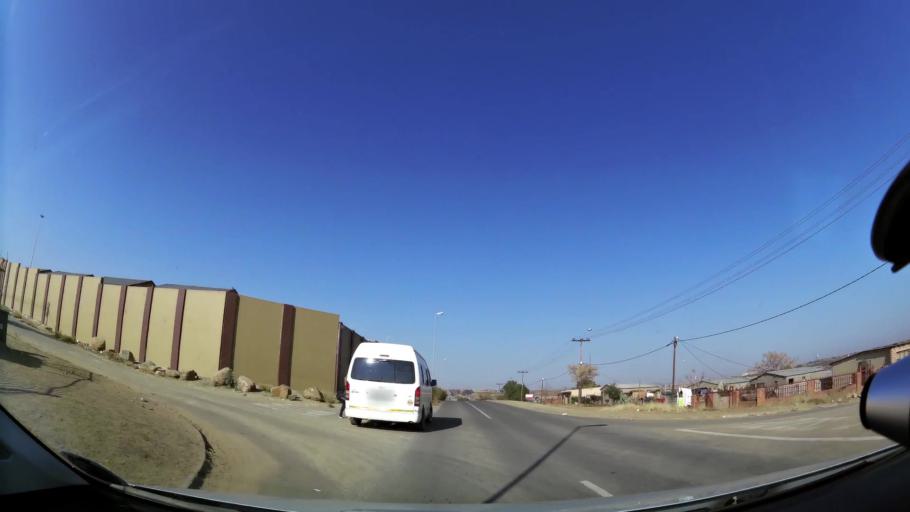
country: ZA
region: Orange Free State
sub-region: Mangaung Metropolitan Municipality
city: Bloemfontein
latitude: -29.1769
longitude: 26.2251
